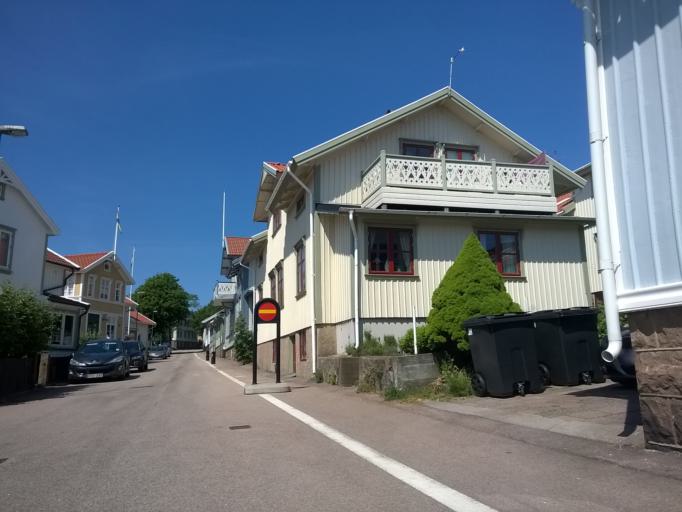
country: SE
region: Vaestra Goetaland
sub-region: Lysekils Kommun
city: Lysekil
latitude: 58.2697
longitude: 11.4329
